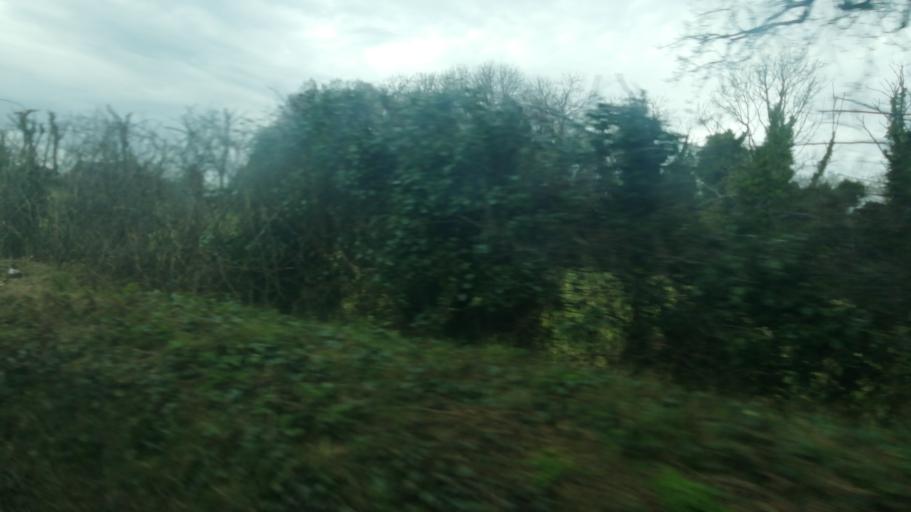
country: IE
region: Leinster
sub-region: Kildare
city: Clane
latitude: 53.3396
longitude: -6.6585
